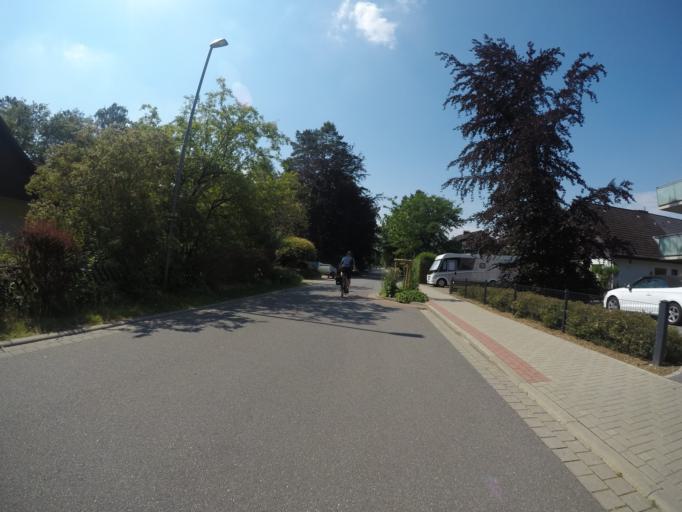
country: DE
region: Lower Saxony
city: Buchholz in der Nordheide
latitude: 53.3273
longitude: 9.8446
